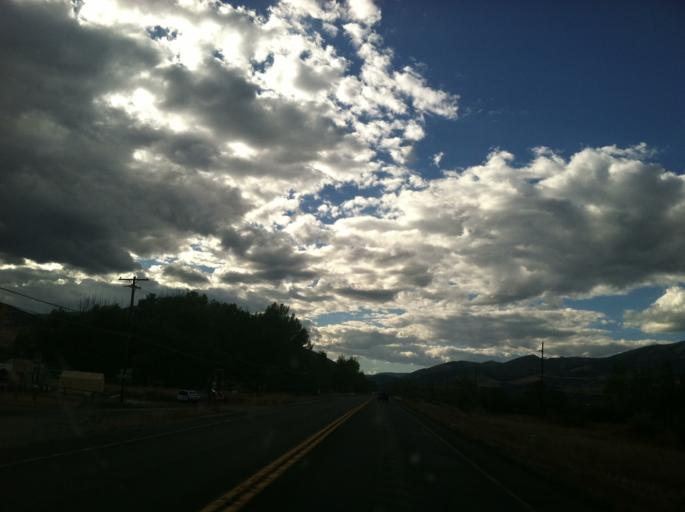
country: US
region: Montana
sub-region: Deer Lodge County
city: Anaconda
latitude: 46.1418
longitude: -112.9903
